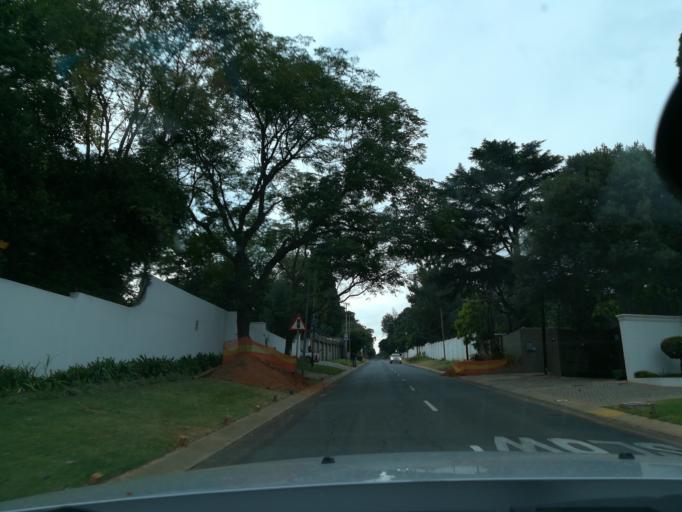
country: ZA
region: Gauteng
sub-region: City of Johannesburg Metropolitan Municipality
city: Diepsloot
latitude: -26.0661
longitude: 27.9940
